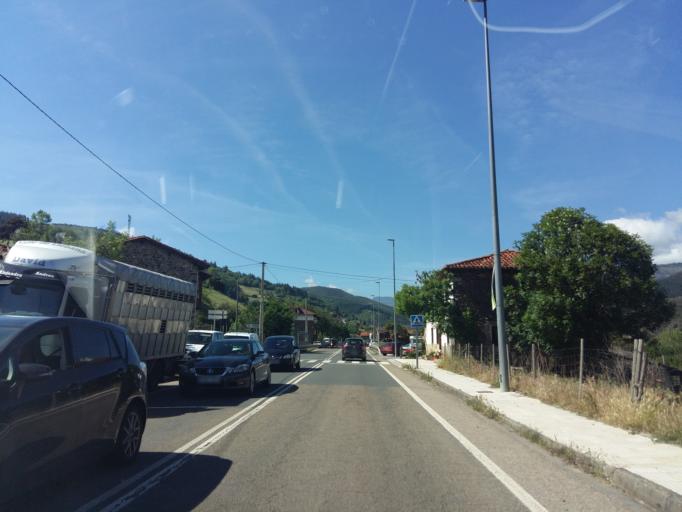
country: ES
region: Cantabria
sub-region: Provincia de Cantabria
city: Potes
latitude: 43.1731
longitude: -4.6012
